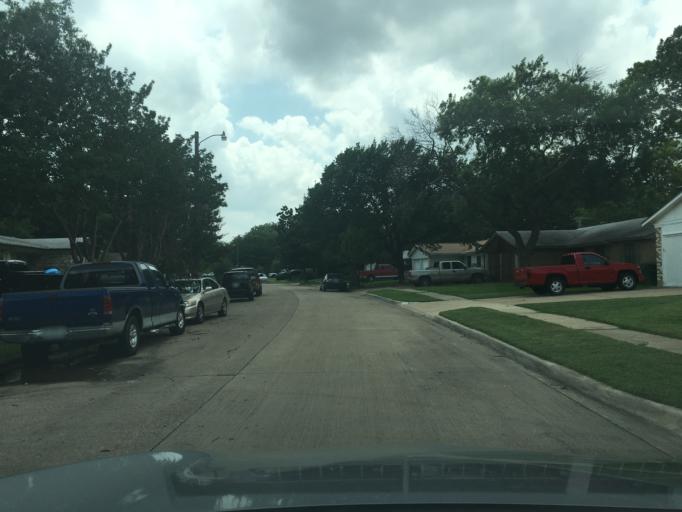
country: US
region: Texas
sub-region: Dallas County
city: Richardson
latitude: 32.9142
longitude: -96.6939
